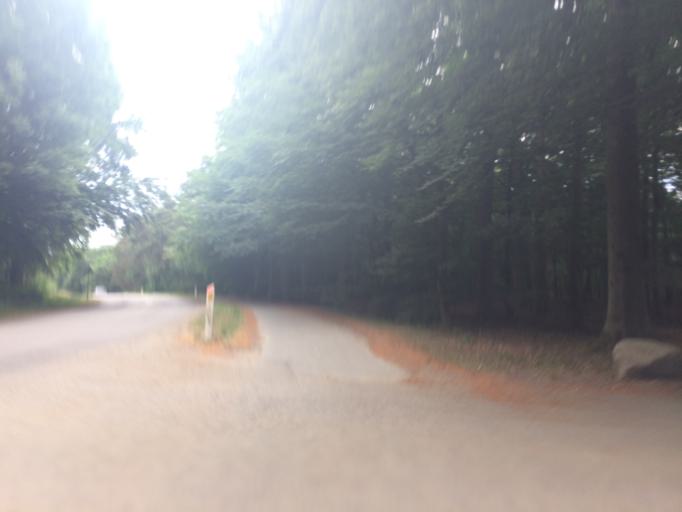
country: DK
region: Capital Region
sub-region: Bornholm Kommune
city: Ronne
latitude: 55.1575
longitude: 14.7146
